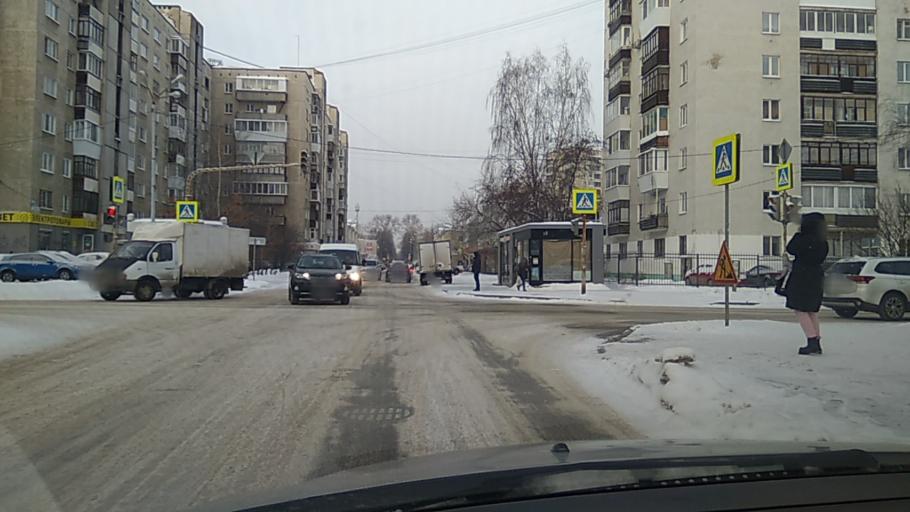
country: RU
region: Sverdlovsk
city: Yekaterinburg
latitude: 56.8970
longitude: 60.5961
